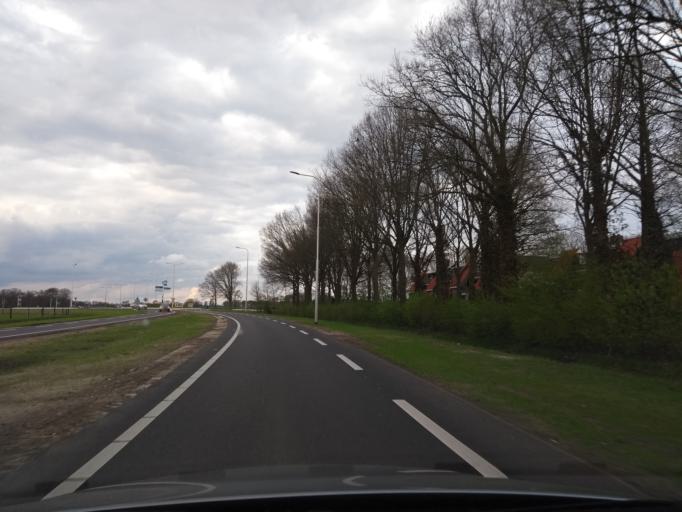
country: NL
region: Overijssel
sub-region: Gemeente Hof van Twente
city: Delden
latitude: 52.2639
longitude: 6.7026
